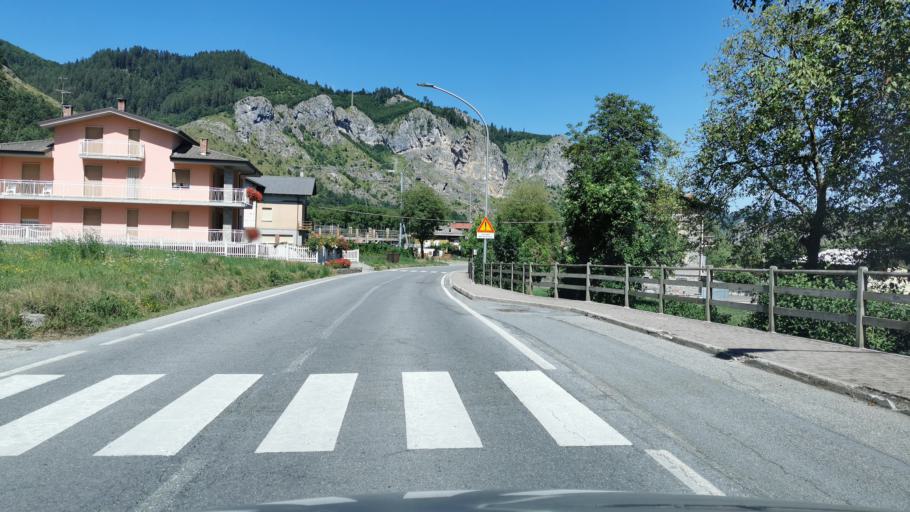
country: IT
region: Piedmont
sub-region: Provincia di Cuneo
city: Valdieri
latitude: 44.2918
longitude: 7.4261
